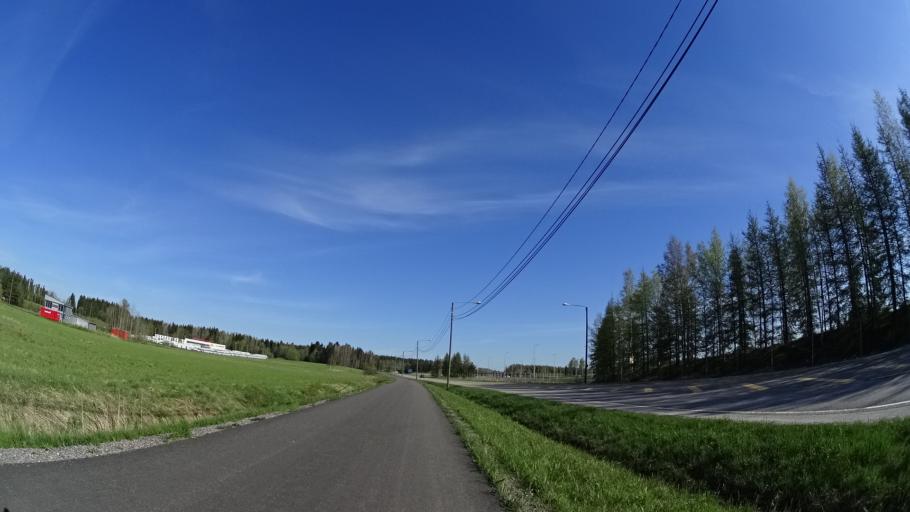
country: FI
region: Uusimaa
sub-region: Helsinki
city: Nurmijaervi
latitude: 60.3494
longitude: 24.8091
